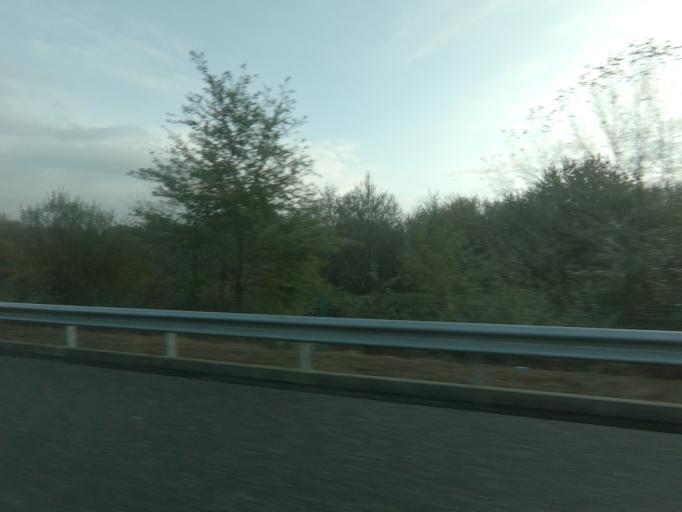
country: ES
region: Galicia
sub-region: Provincia de Pontevedra
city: Tui
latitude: 42.0920
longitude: -8.6427
